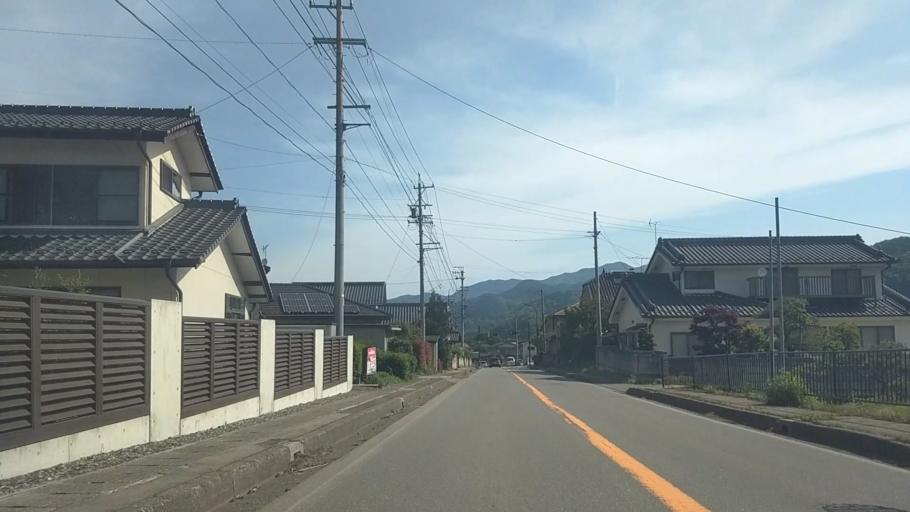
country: JP
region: Nagano
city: Saku
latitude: 36.0755
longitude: 138.4777
